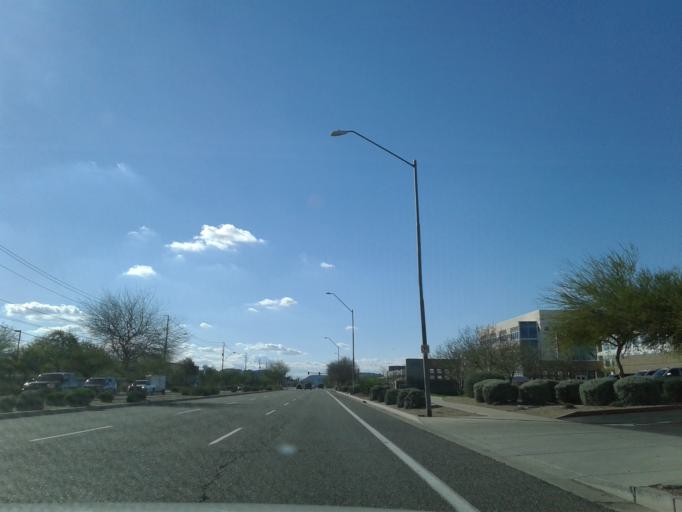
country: US
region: Arizona
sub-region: Maricopa County
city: Glendale
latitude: 33.6839
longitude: -112.0938
